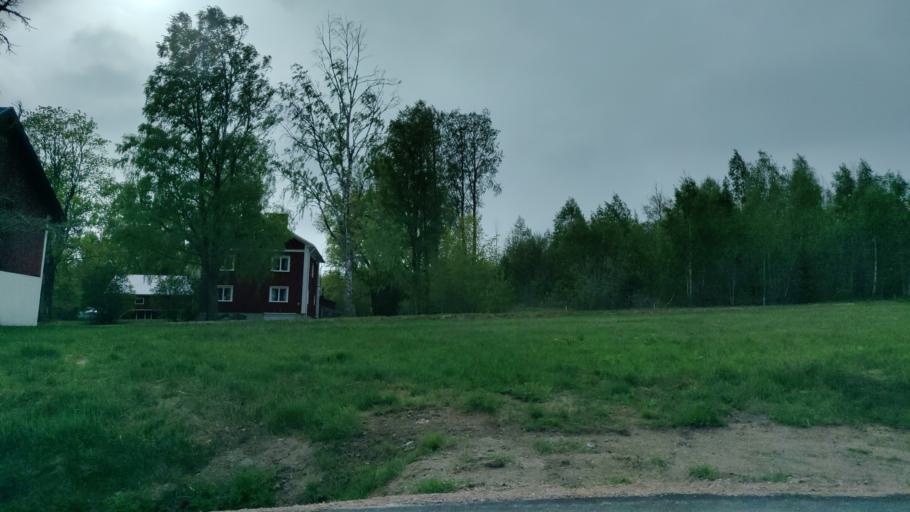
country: SE
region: Vaermland
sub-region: Forshaga Kommun
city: Deje
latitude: 59.6453
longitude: 13.4433
